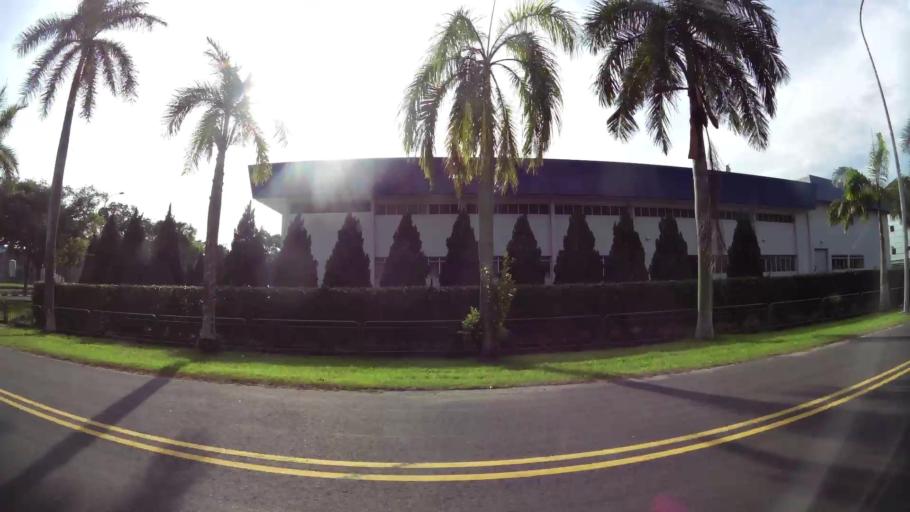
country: MY
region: Johor
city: Johor Bahru
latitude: 1.3367
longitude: 103.6447
